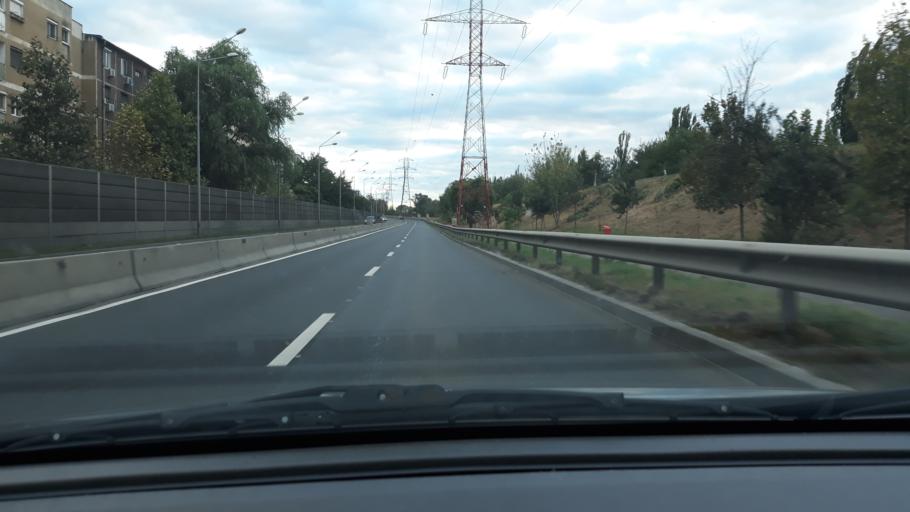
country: RO
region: Bihor
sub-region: Comuna Biharea
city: Oradea
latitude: 47.0784
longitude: 21.9097
